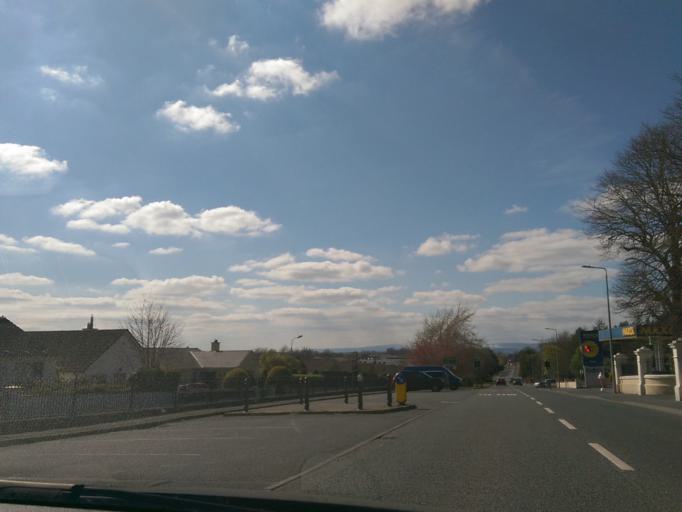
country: IE
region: Leinster
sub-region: Laois
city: Portlaoise
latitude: 53.0329
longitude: -7.2723
